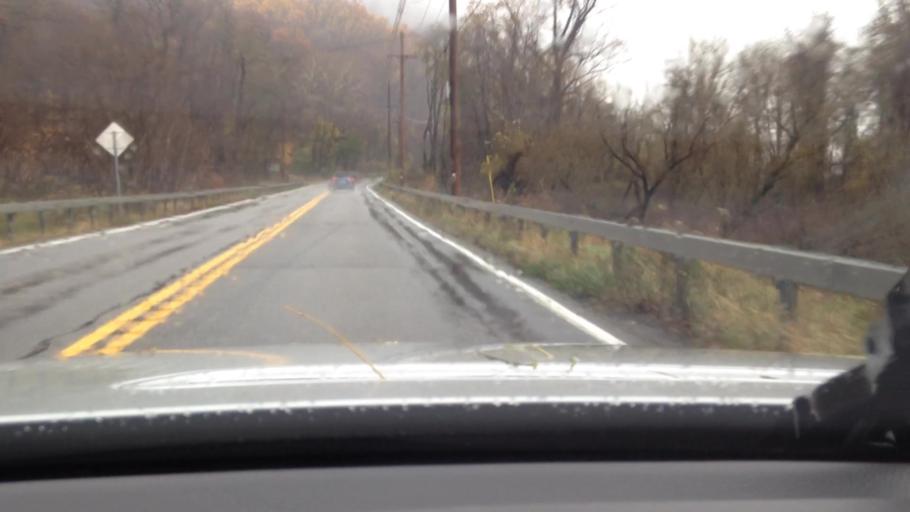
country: US
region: New York
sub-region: Putnam County
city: Cold Spring
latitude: 41.4405
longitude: -73.9746
